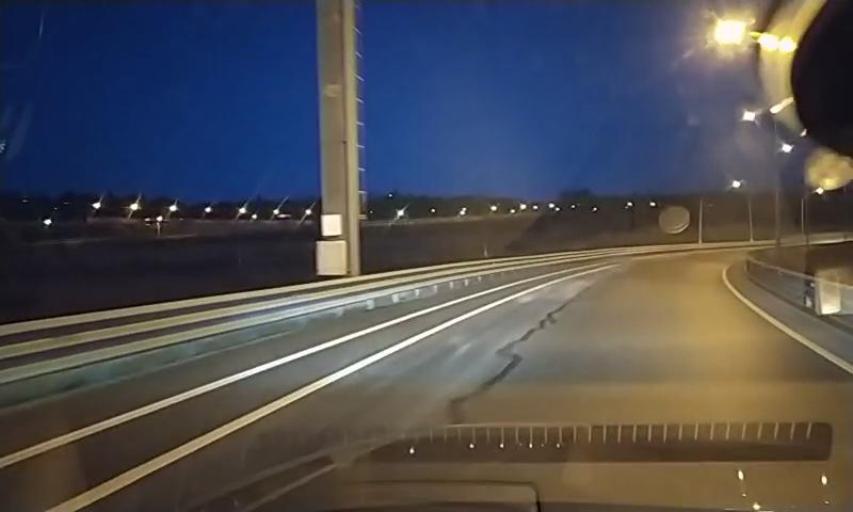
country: RU
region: St.-Petersburg
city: Beloostrov
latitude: 60.1498
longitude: 29.9824
